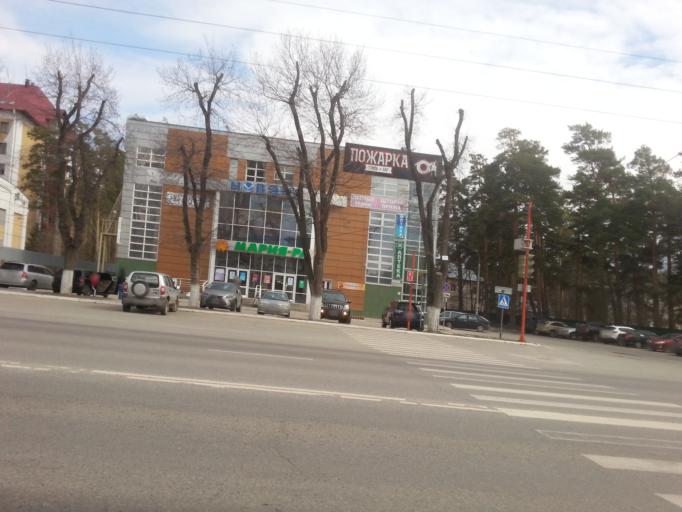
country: RU
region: Altai Krai
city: Zaton
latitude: 53.2863
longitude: 83.7539
